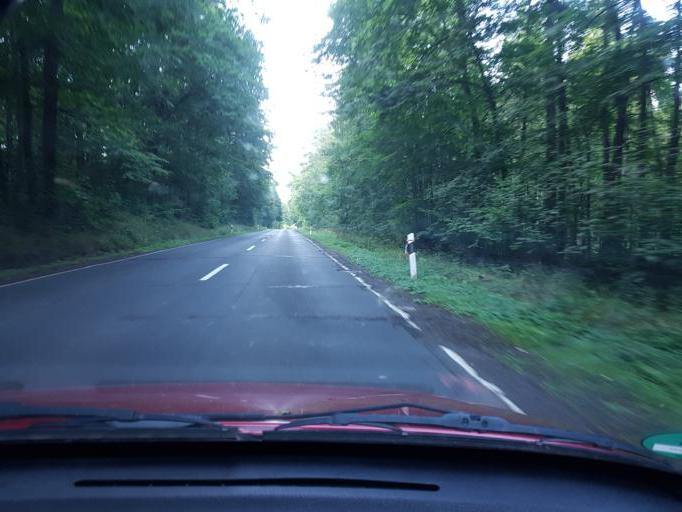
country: DE
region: Hesse
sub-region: Regierungsbezirk Giessen
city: Alten Buseck
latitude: 50.5864
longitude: 8.7310
